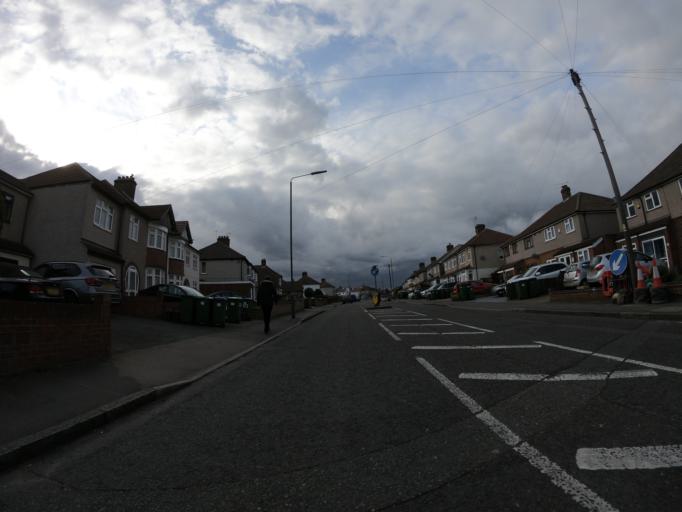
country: GB
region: England
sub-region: Greater London
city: Bexleyheath
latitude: 51.4728
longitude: 0.1496
